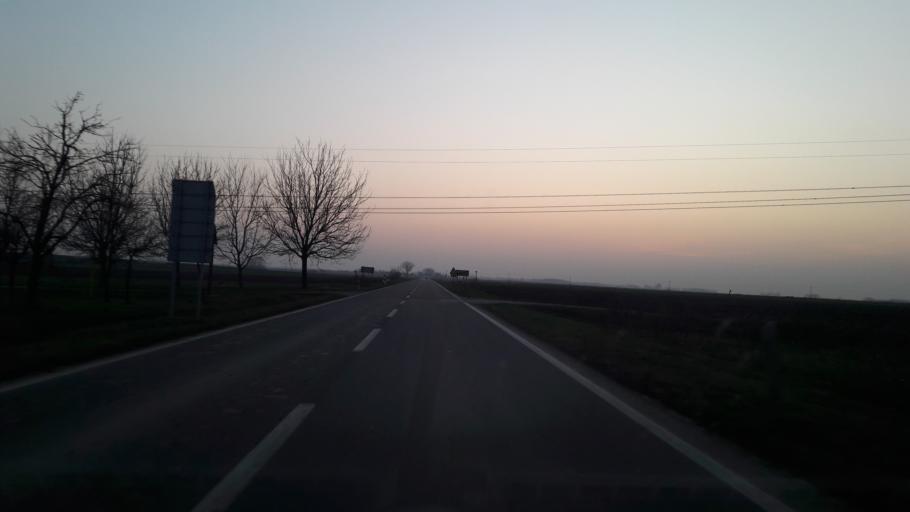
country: HR
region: Vukovarsko-Srijemska
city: Negoslavci
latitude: 45.2695
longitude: 18.9960
